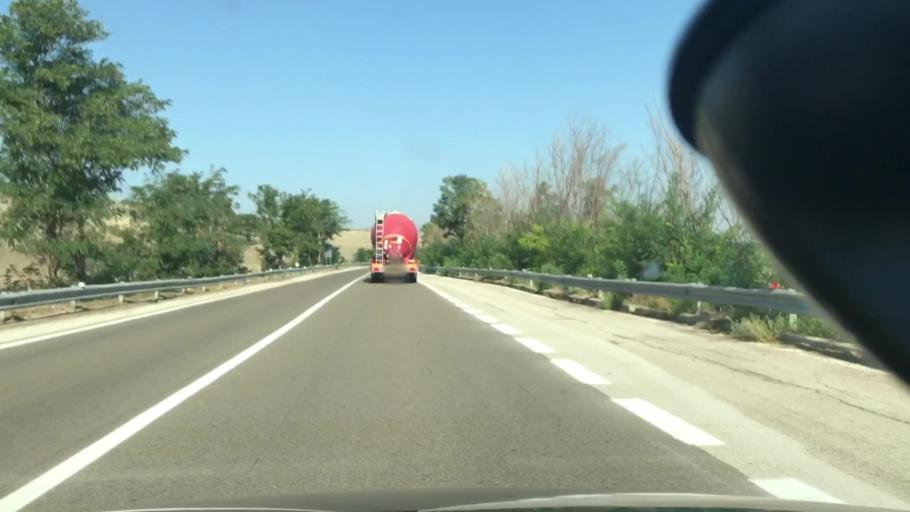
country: IT
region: Basilicate
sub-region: Provincia di Matera
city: Irsina
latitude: 40.7932
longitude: 16.2794
